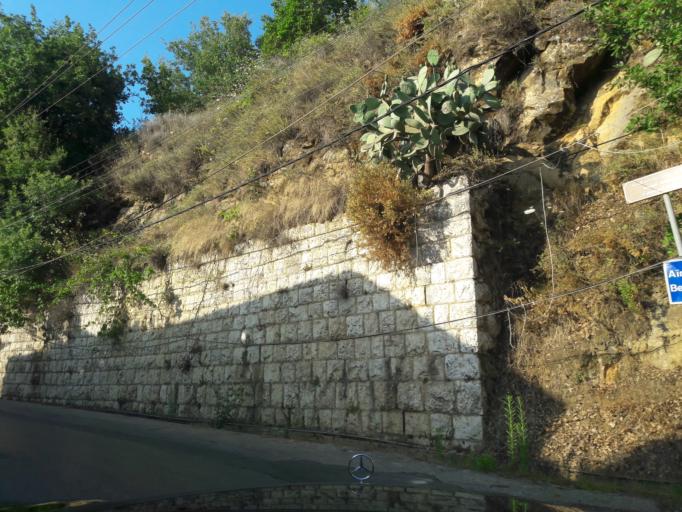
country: LB
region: Mont-Liban
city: Djounie
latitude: 33.9257
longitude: 35.6729
